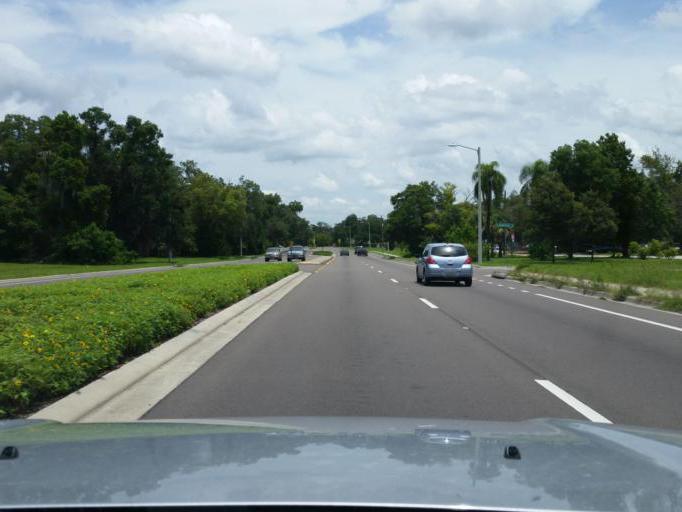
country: US
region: Florida
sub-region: Hillsborough County
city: Temple Terrace
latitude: 28.0143
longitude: -82.4147
